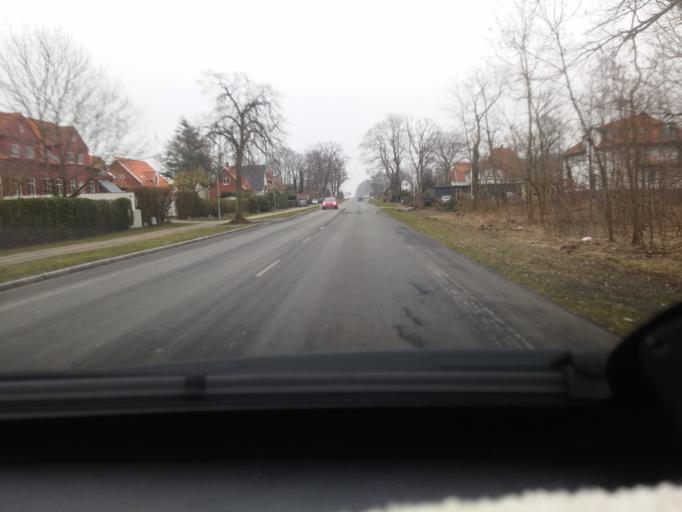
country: DK
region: South Denmark
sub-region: Kerteminde Kommune
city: Kerteminde
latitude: 55.4452
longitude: 10.6653
